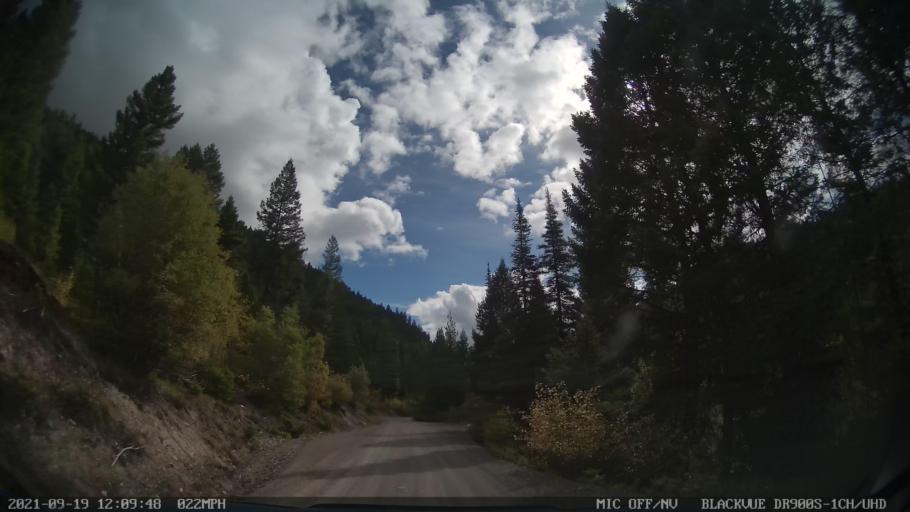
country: US
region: Montana
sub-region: Missoula County
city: Seeley Lake
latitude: 47.1818
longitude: -113.3887
